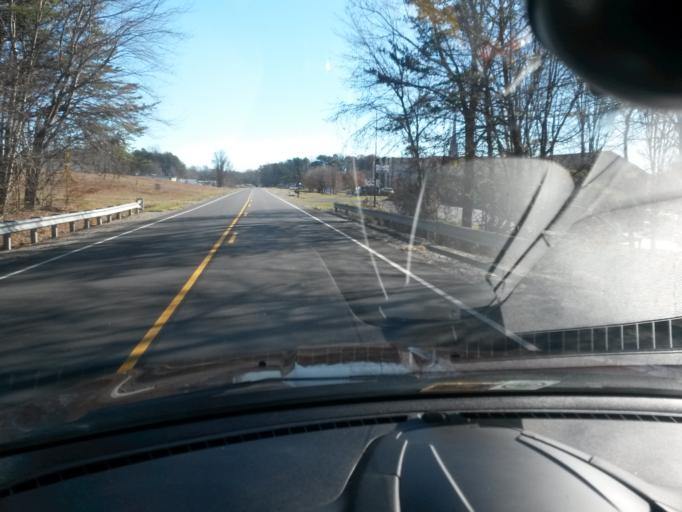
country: US
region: Virginia
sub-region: Henry County
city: Pannill Fork
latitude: 36.7525
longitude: -80.0848
